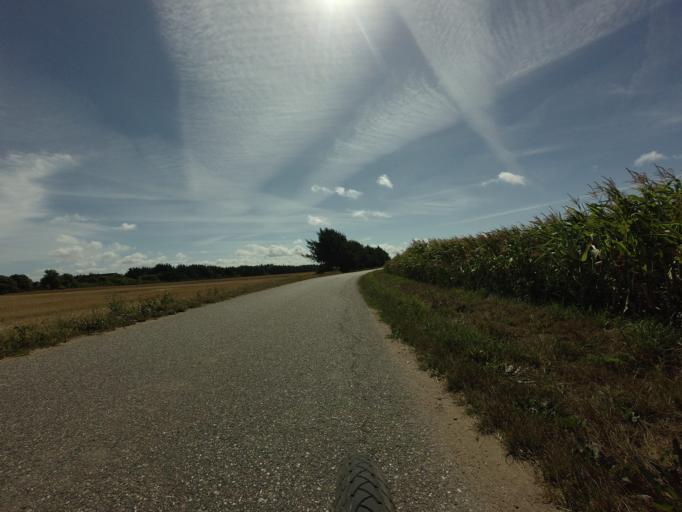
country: DK
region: North Denmark
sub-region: Hjorring Kommune
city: Vra
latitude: 57.3809
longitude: 9.7840
